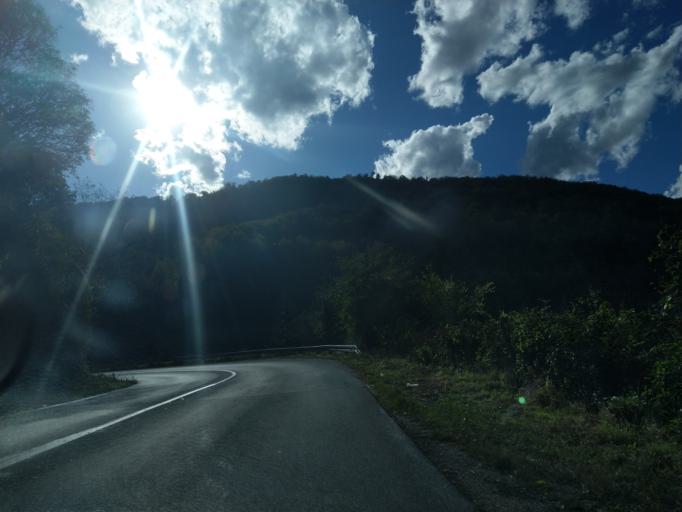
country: RS
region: Central Serbia
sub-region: Zlatiborski Okrug
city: Uzice
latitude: 43.8747
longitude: 19.7934
